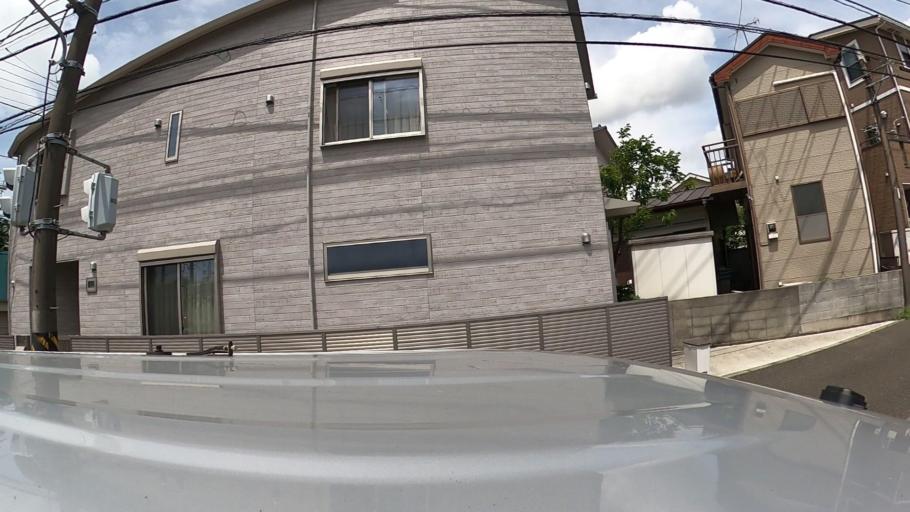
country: JP
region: Kanagawa
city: Fujisawa
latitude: 35.4093
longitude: 139.4698
